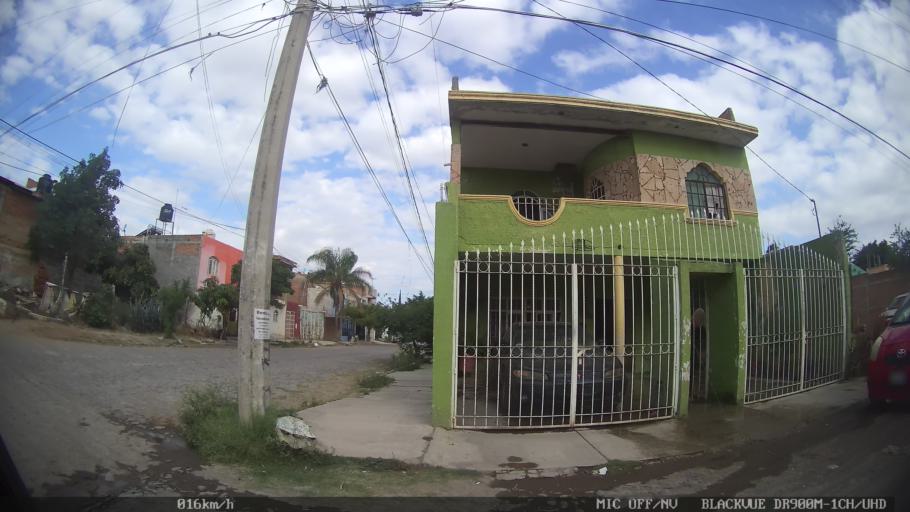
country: MX
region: Jalisco
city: Tonala
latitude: 20.6597
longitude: -103.2395
